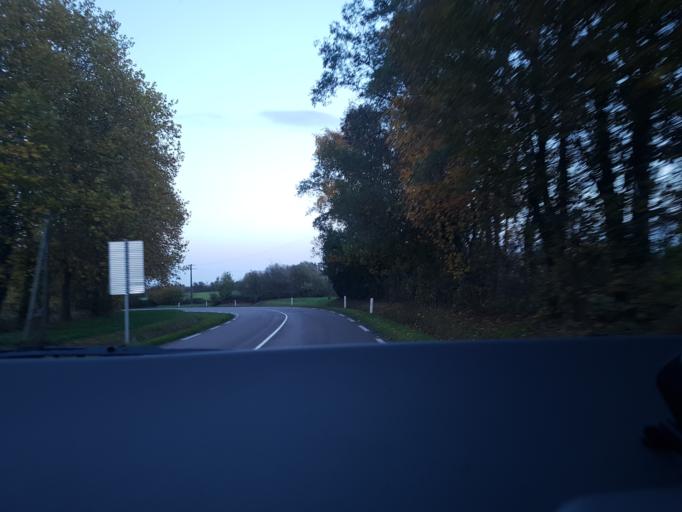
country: FR
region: Haute-Normandie
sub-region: Departement de l'Eure
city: Beuzeville
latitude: 49.3446
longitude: 0.3616
